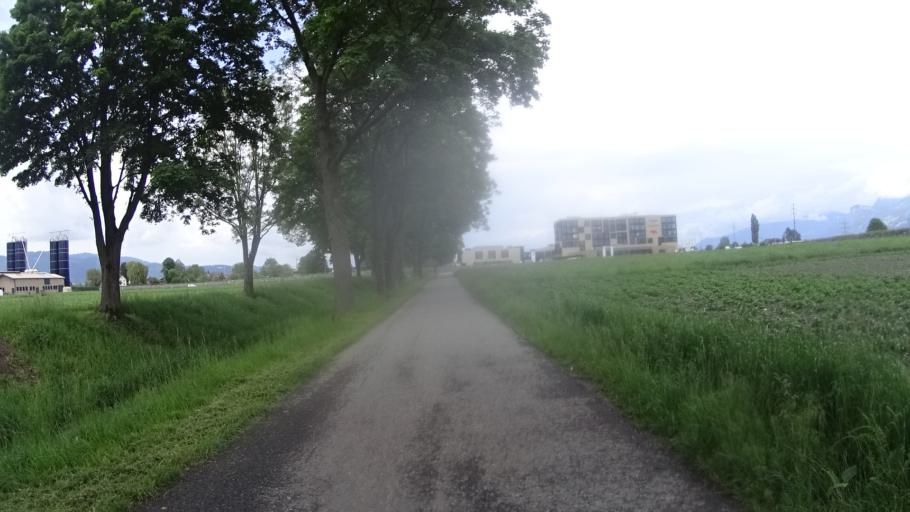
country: AT
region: Vorarlberg
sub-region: Politischer Bezirk Feldkirch
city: Mader
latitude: 47.3570
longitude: 9.6045
